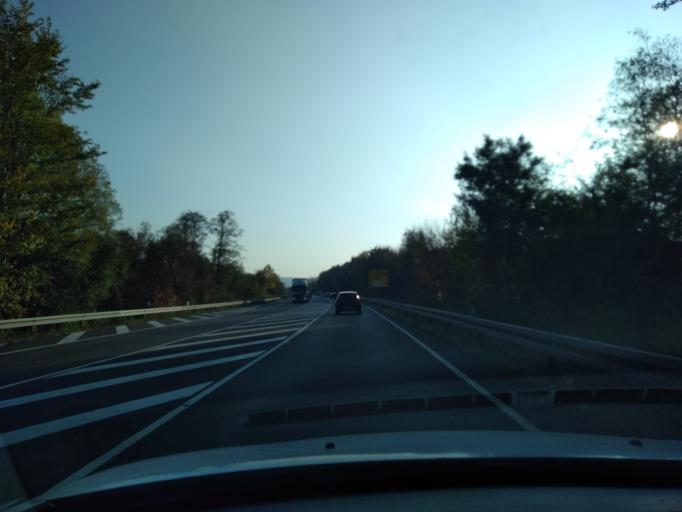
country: FR
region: Lorraine
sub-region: Departement de la Moselle
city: Grosbliederstroff
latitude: 49.1747
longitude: 7.0296
